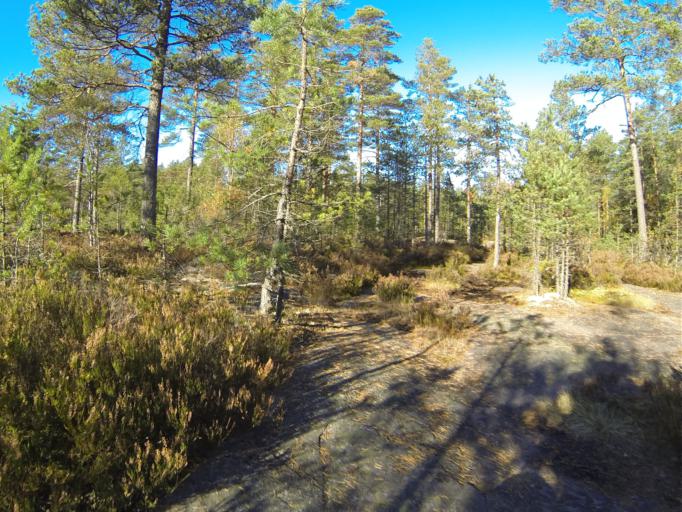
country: FI
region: Varsinais-Suomi
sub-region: Salo
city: Saerkisalo
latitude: 60.2033
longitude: 22.9230
